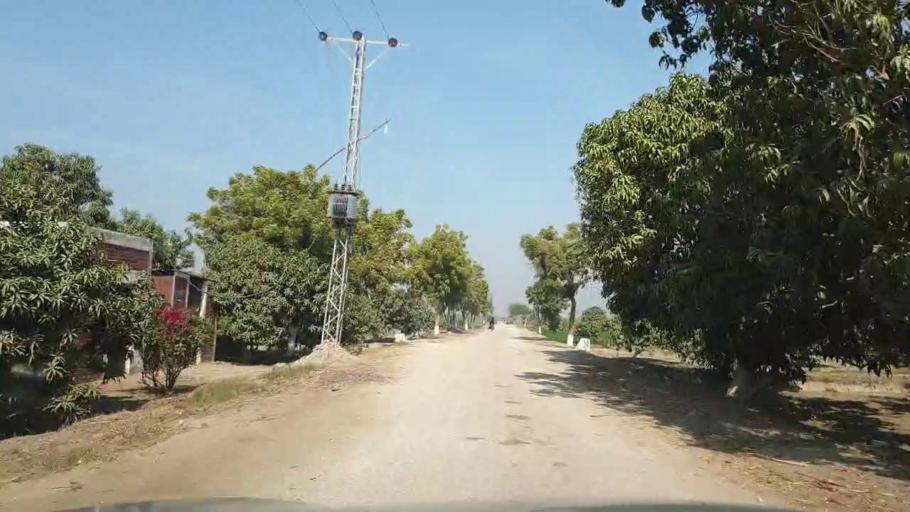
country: PK
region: Sindh
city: Tando Adam
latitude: 25.6280
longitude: 68.7383
